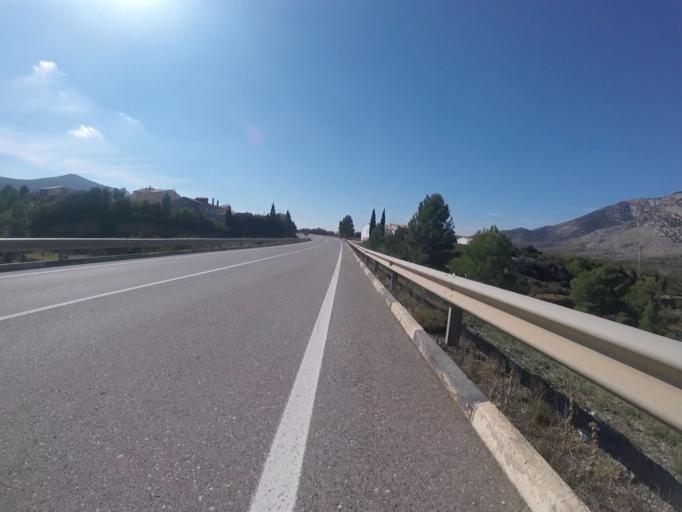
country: ES
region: Valencia
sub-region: Provincia de Castello
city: Sierra-Engarceran
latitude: 40.2994
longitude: -0.0465
